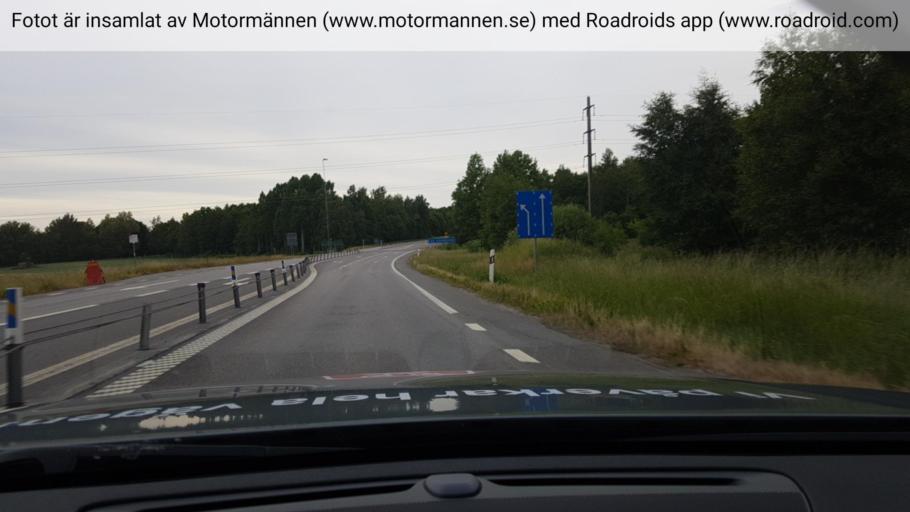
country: SE
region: OEstergoetland
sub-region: Motala Kommun
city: Motala
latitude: 58.5647
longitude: 15.0643
